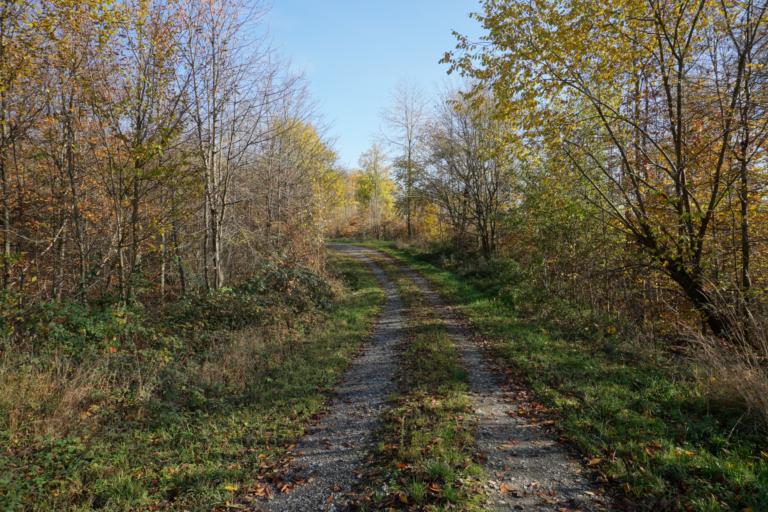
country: DE
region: Baden-Wuerttemberg
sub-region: Karlsruhe Region
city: Aglasterhausen
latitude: 49.3650
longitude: 8.9981
